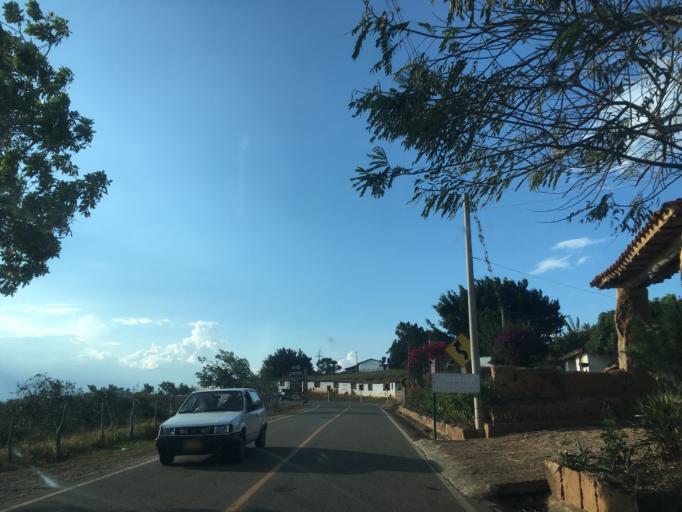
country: CO
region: Santander
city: Villanueva
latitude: 6.6304
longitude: -73.1771
